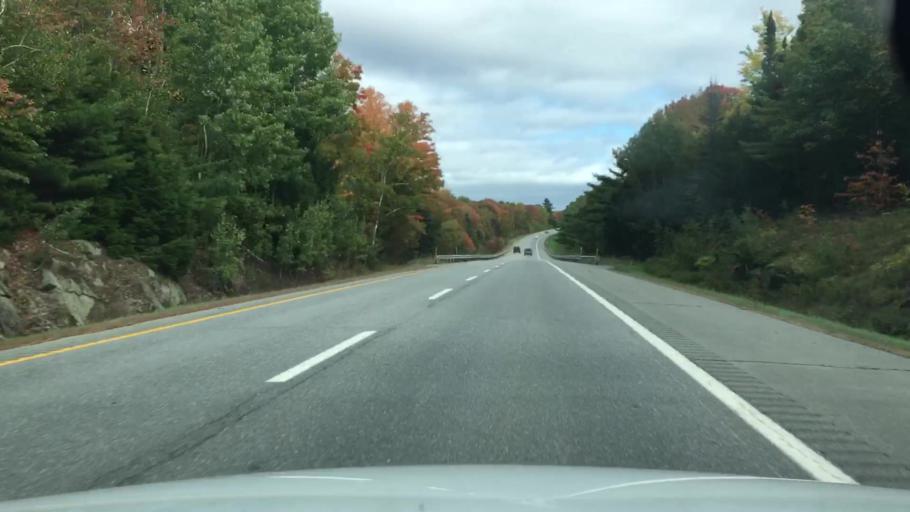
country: US
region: Maine
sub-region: Penobscot County
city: Carmel
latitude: 44.7733
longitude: -69.0195
